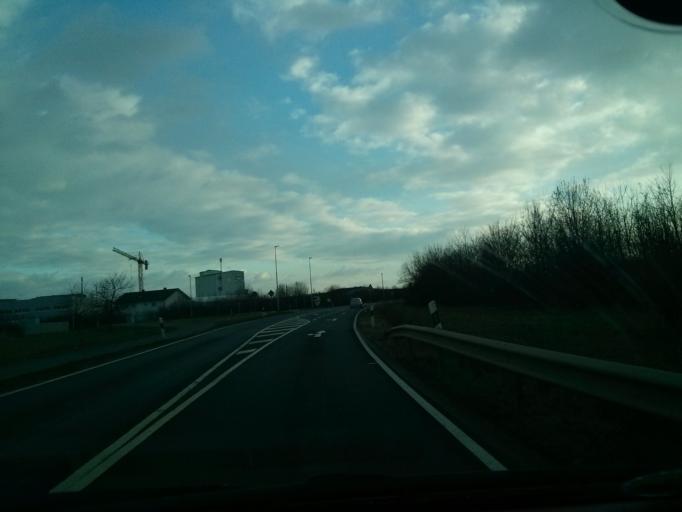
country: DE
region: North Rhine-Westphalia
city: Meckenheim
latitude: 50.6507
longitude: 7.0138
